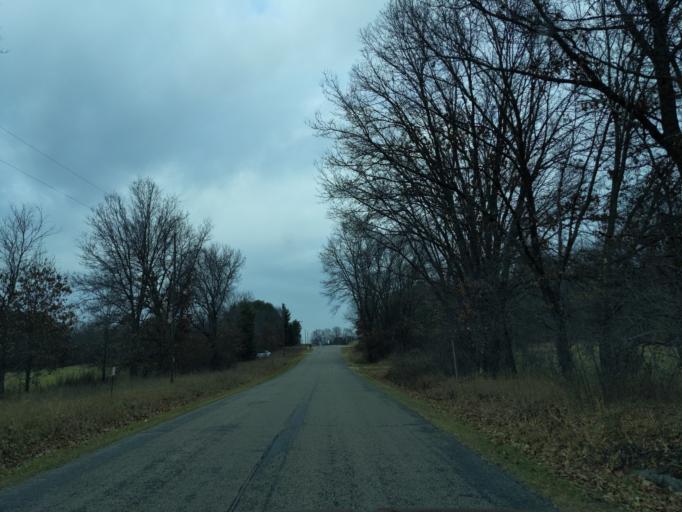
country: US
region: Wisconsin
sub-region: Waushara County
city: Wautoma
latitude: 44.0468
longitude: -89.2774
